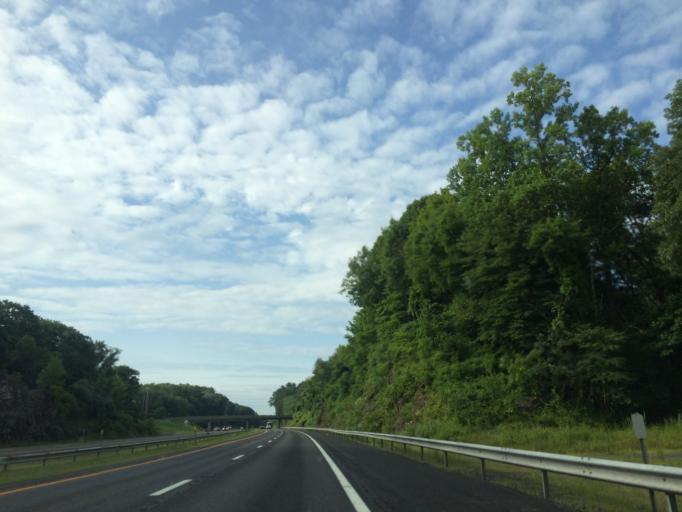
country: US
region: New York
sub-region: Ulster County
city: Rosendale Village
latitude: 41.8718
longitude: -74.0584
